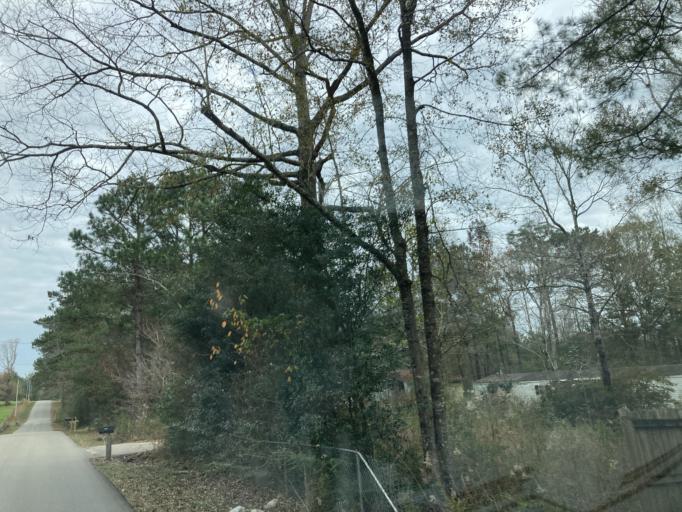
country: US
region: Mississippi
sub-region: Perry County
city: New Augusta
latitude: 31.0654
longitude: -89.2042
